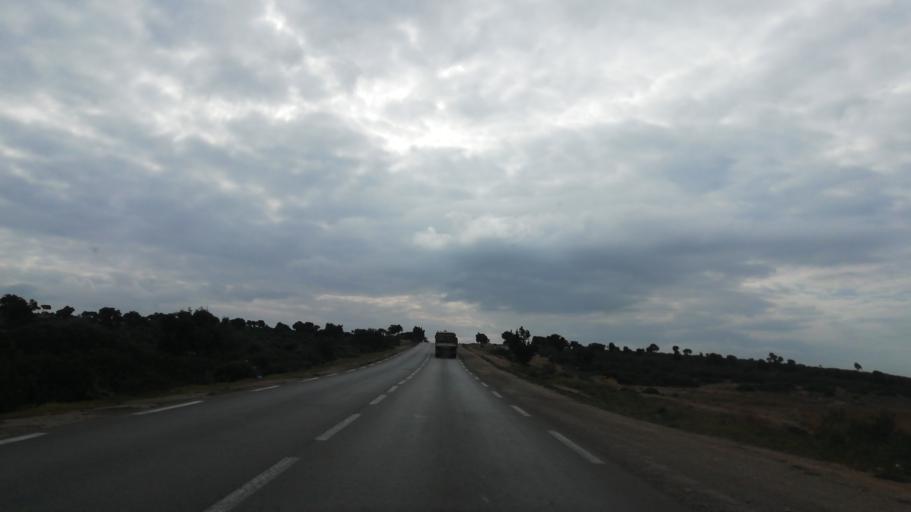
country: DZ
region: Oran
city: Ain el Bya
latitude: 35.7324
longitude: -0.3550
